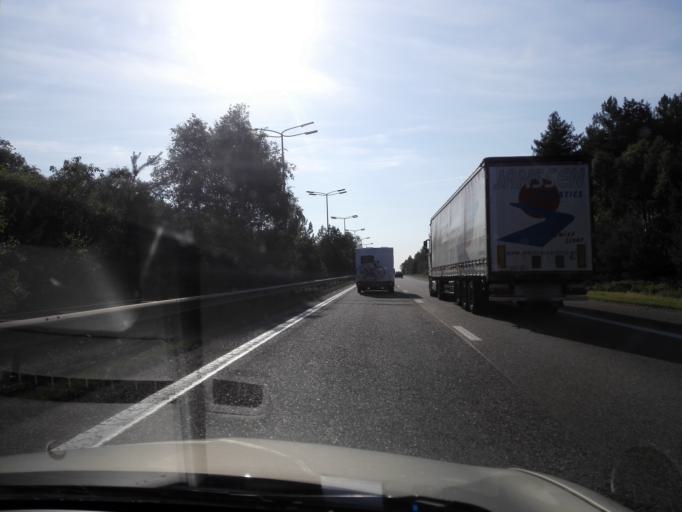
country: BE
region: Flanders
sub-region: Provincie Limburg
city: Houthalen
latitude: 51.0111
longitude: 5.4146
